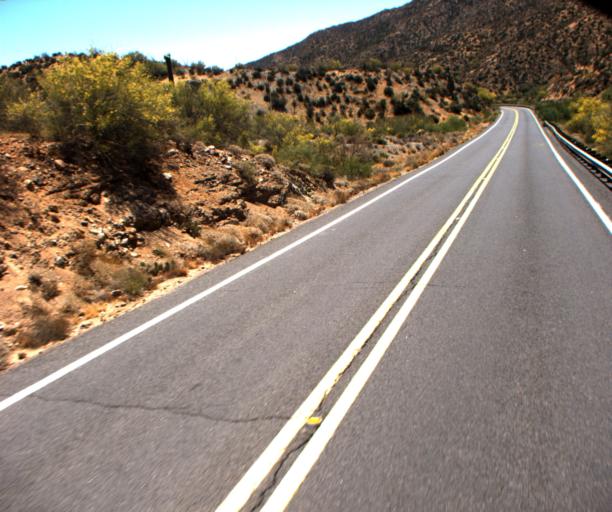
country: US
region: Arizona
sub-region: Pinal County
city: Superior
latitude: 33.1778
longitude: -111.0373
